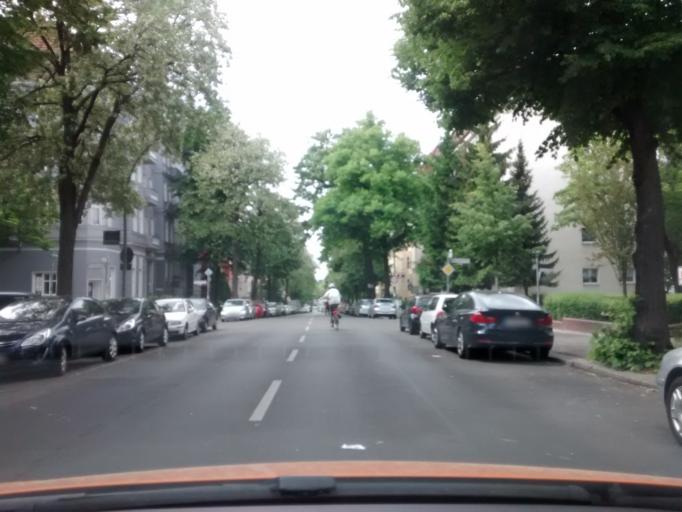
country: DE
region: Berlin
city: Lankwitz
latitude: 52.4491
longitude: 13.3454
